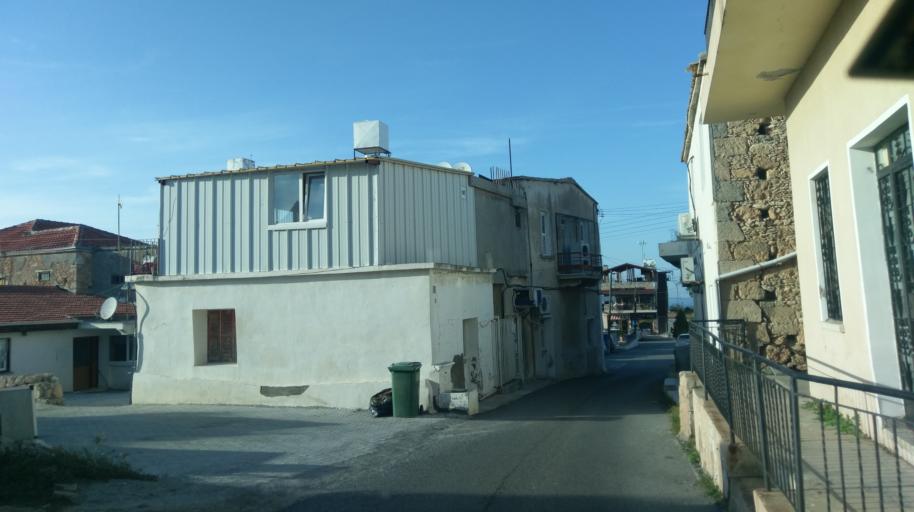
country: CY
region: Ammochostos
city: Lefkonoiko
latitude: 35.3398
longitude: 33.5809
